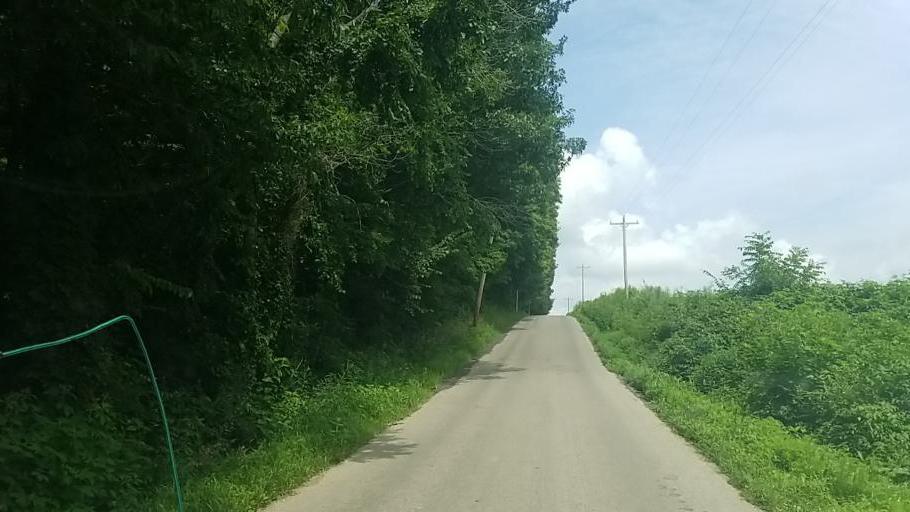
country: US
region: Ohio
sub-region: Knox County
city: Oak Hill
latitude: 40.3091
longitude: -82.2599
